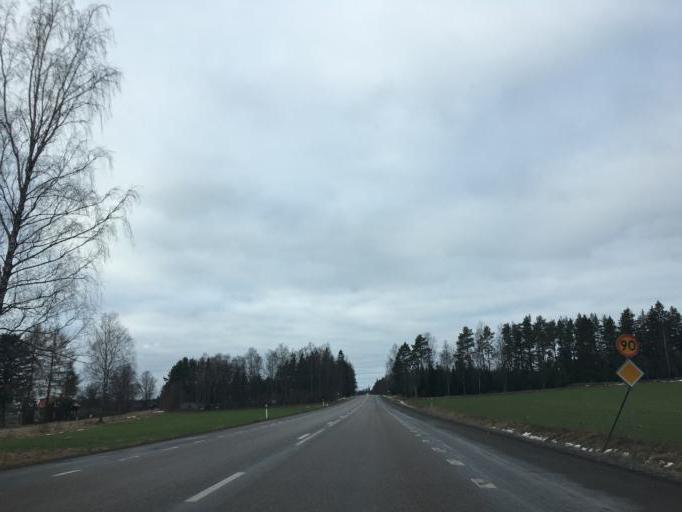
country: SE
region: Soedermanland
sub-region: Nykopings Kommun
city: Stigtomta
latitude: 58.7858
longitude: 16.8142
